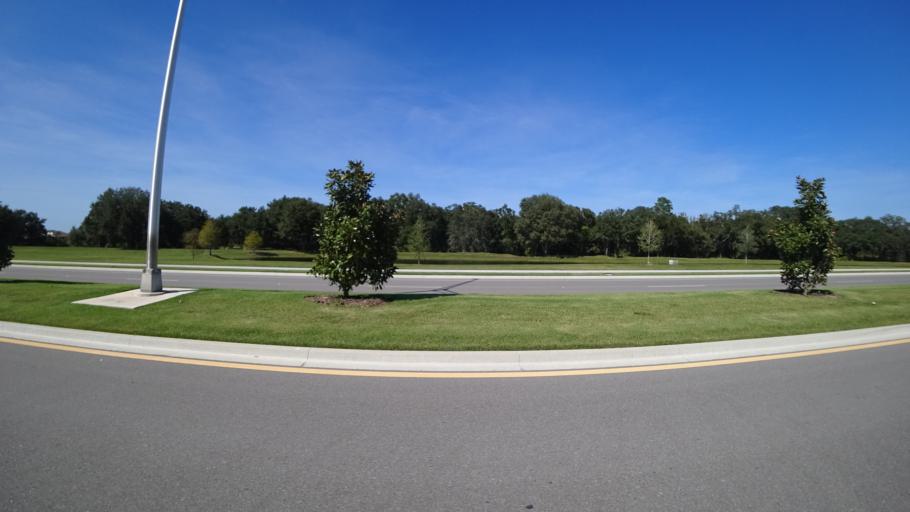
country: US
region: Florida
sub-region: Sarasota County
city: The Meadows
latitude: 27.4011
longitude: -82.3649
